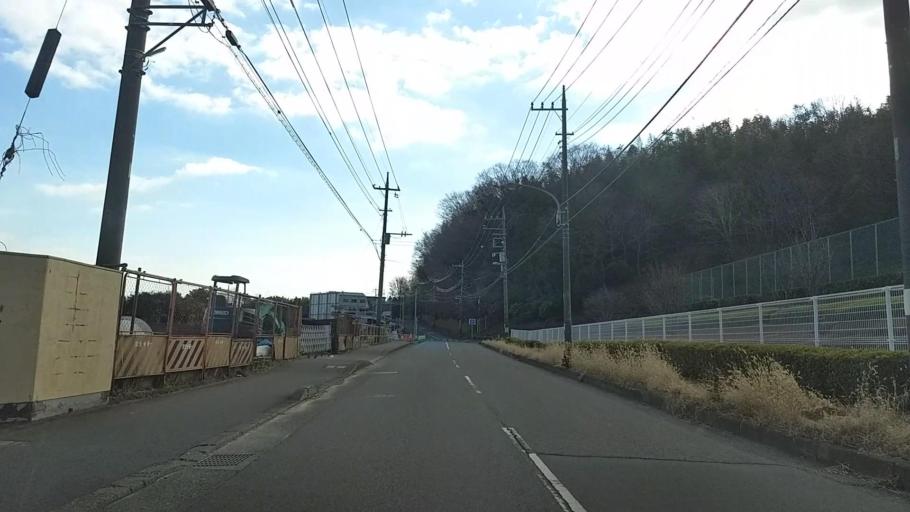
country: JP
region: Kanagawa
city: Atsugi
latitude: 35.4293
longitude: 139.3256
